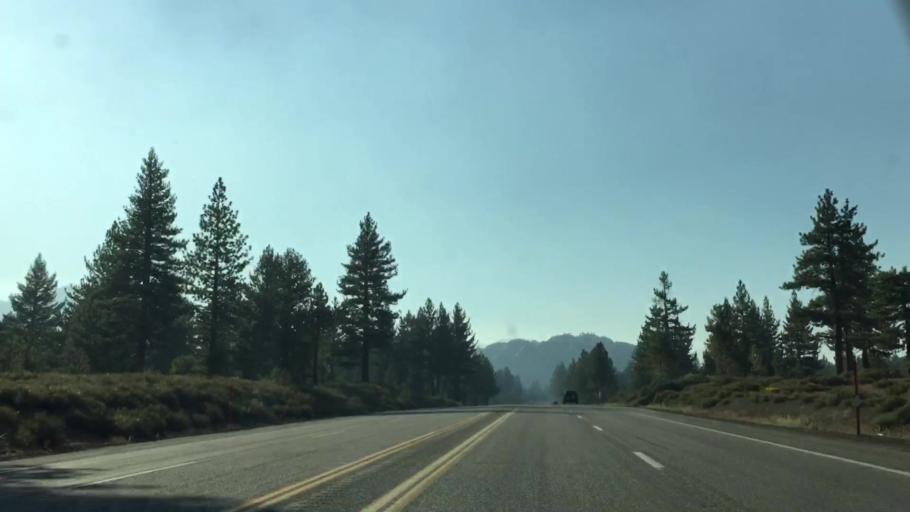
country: US
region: California
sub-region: Mono County
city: Mammoth Lakes
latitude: 37.7713
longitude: -119.0087
